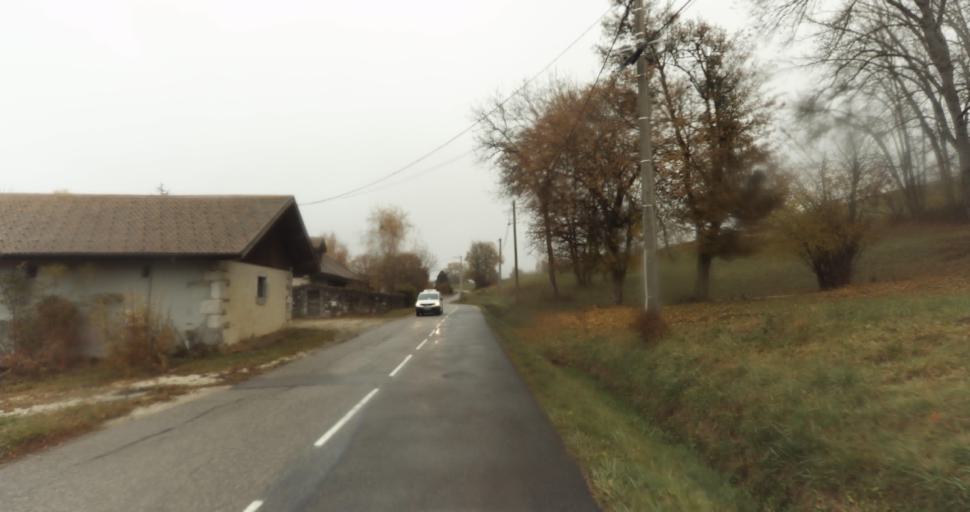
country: FR
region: Rhone-Alpes
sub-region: Departement de la Haute-Savoie
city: Thorens-Glieres
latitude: 45.9819
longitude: 6.2285
